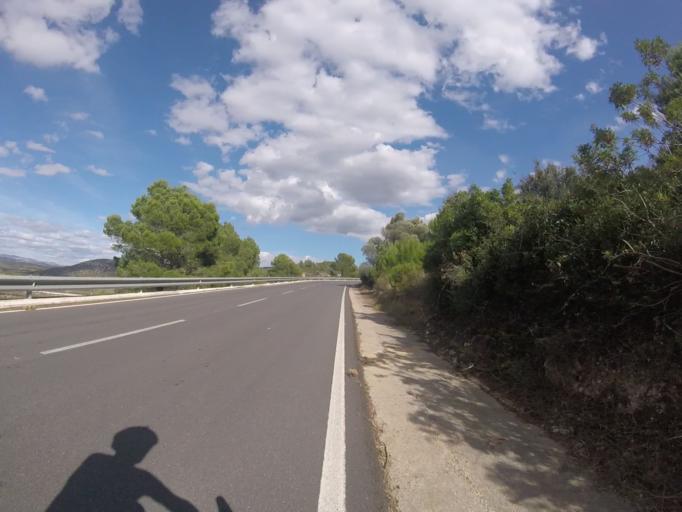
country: ES
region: Valencia
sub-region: Provincia de Castello
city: Cuevas de Vinroma
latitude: 40.3201
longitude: 0.1320
